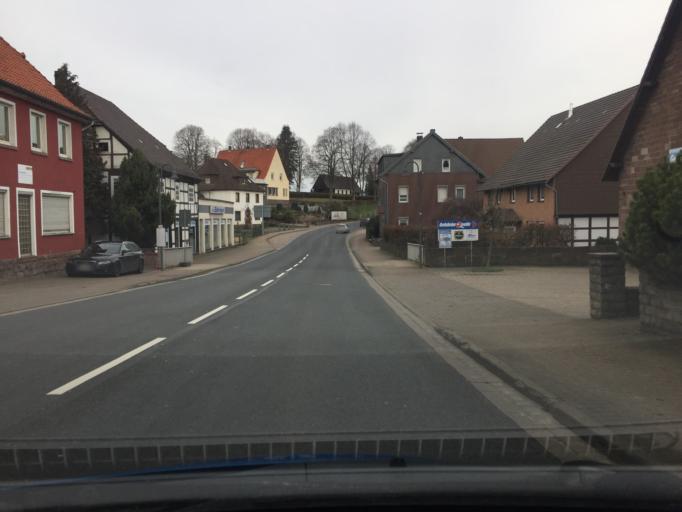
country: DE
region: Lower Saxony
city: Eschershausen
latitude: 51.9300
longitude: 9.6339
